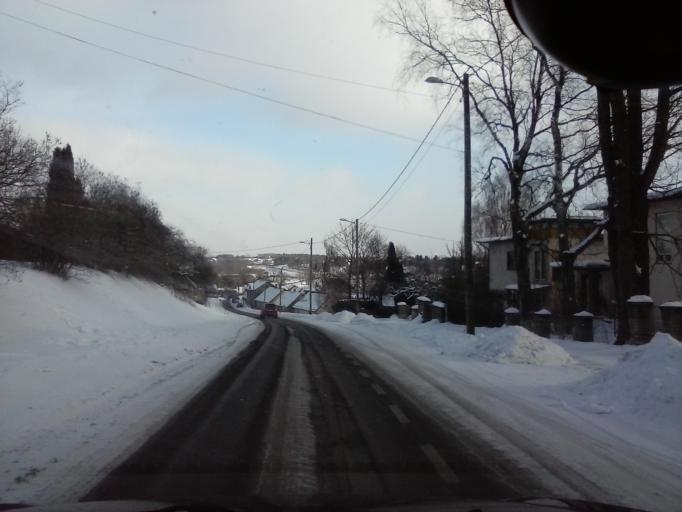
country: EE
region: Viljandimaa
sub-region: Viljandi linn
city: Viljandi
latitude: 58.3654
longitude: 25.6137
